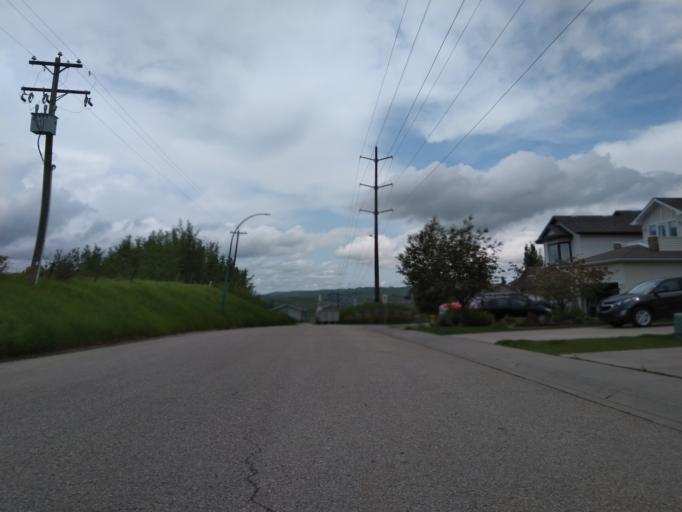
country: CA
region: Alberta
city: Cochrane
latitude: 51.1856
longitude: -114.5132
